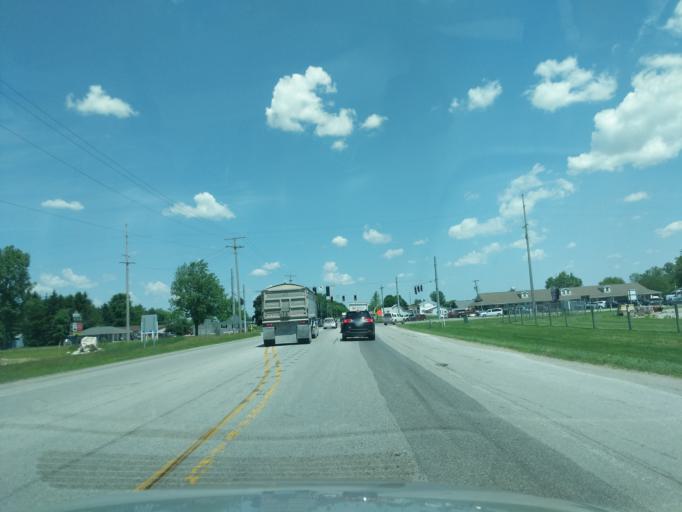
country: US
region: Indiana
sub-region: LaGrange County
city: Topeka
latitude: 41.6536
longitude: -85.5802
